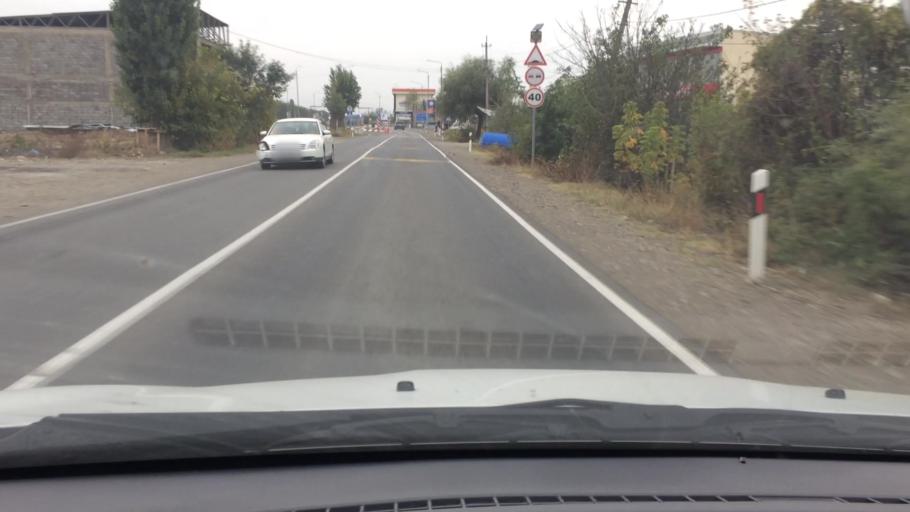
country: GE
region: Kvemo Kartli
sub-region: Marneuli
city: Marneuli
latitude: 41.4615
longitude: 44.8094
